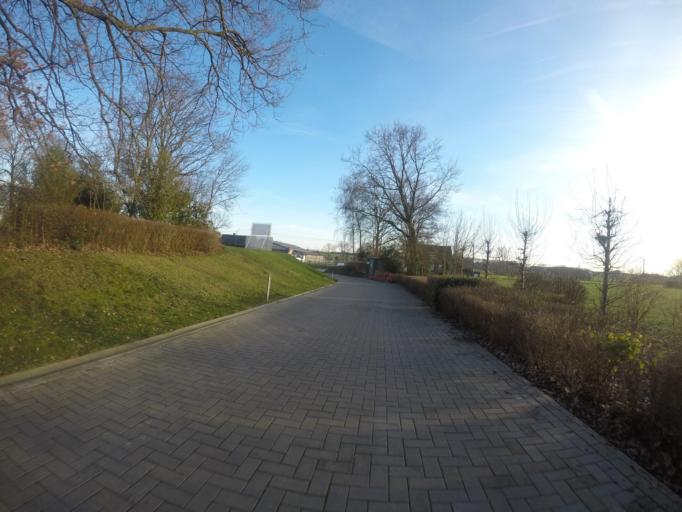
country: BE
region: Flanders
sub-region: Provincie Vlaams-Brabant
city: Pepingen
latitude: 50.7609
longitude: 4.1787
